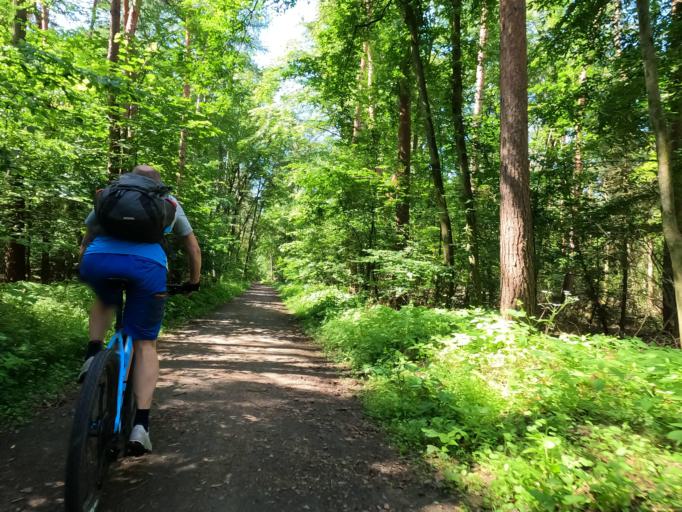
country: DE
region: Hesse
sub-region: Regierungsbezirk Darmstadt
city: Offenbach
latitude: 50.0766
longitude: 8.7423
